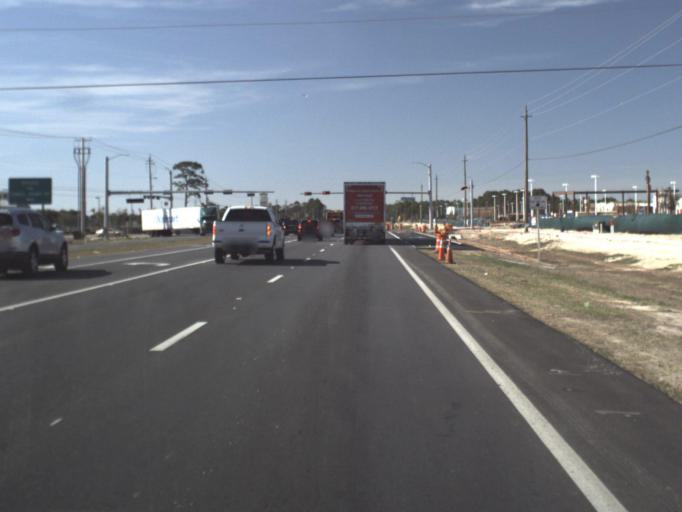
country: US
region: Florida
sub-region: Bay County
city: Laguna Beach
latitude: 30.2200
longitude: -85.8645
